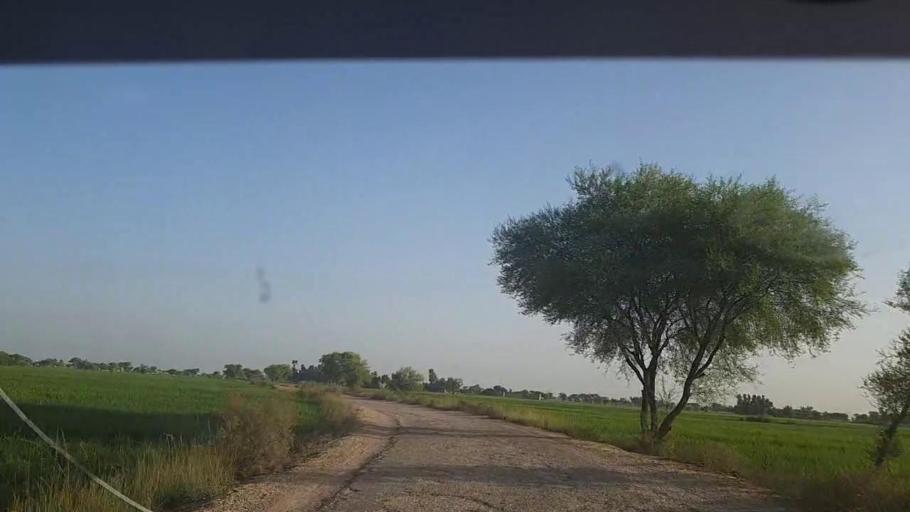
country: PK
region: Sindh
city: Thul
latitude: 28.2093
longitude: 68.8703
